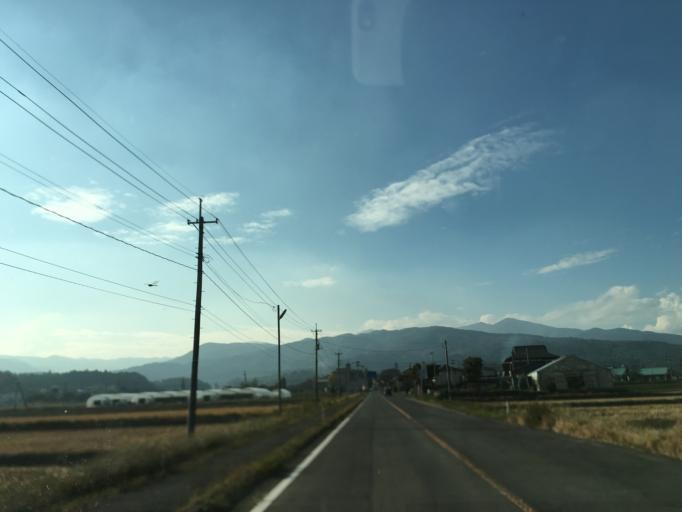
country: JP
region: Fukushima
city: Koriyama
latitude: 37.4164
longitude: 140.2793
